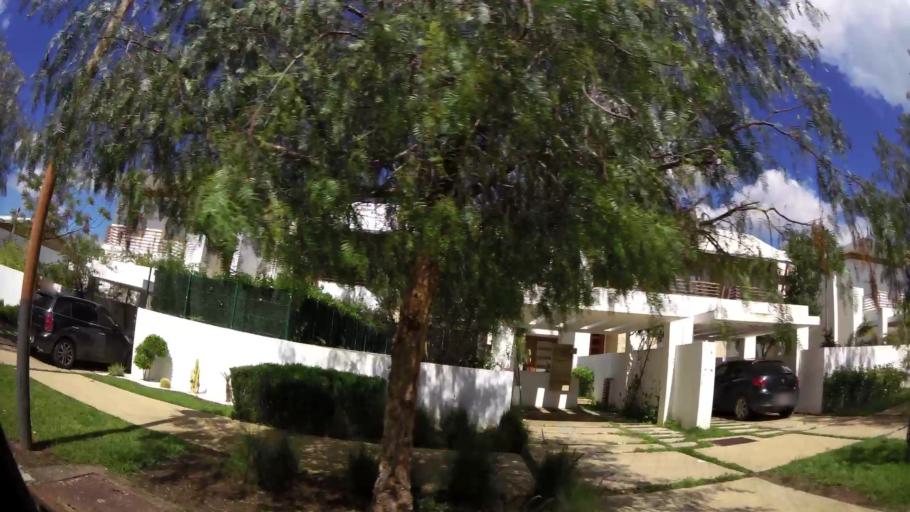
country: MA
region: Grand Casablanca
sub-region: Mediouna
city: Mediouna
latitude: 33.4885
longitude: -7.5828
